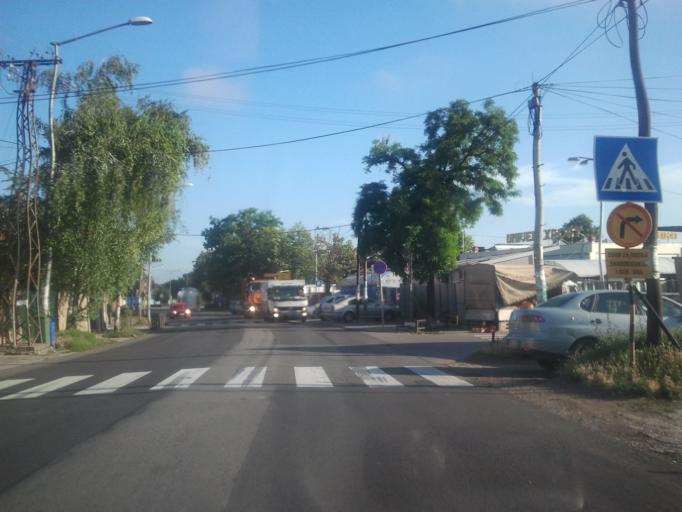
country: RS
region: Autonomna Pokrajina Vojvodina
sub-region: Juznobacki Okrug
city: Petrovaradin
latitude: 45.2409
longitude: 19.8831
